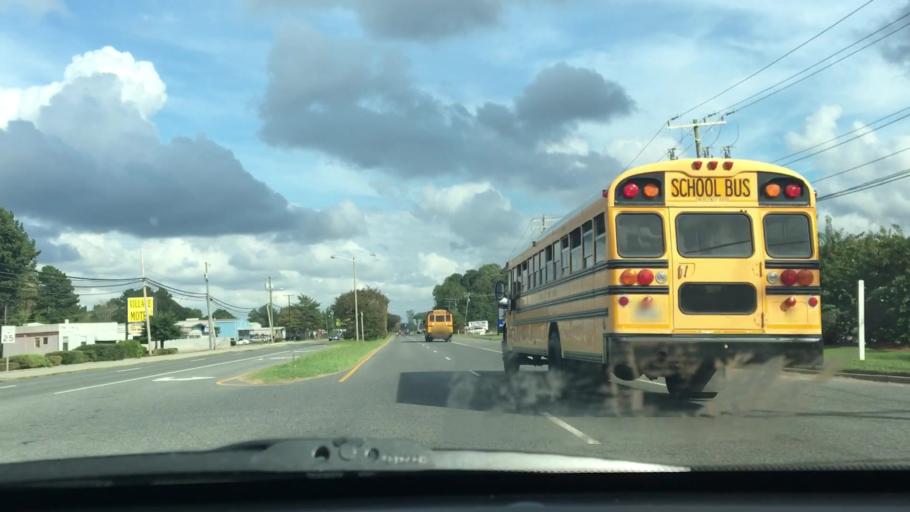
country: US
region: Virginia
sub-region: City of Portsmouth
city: Portsmouth Heights
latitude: 36.7726
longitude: -76.3359
